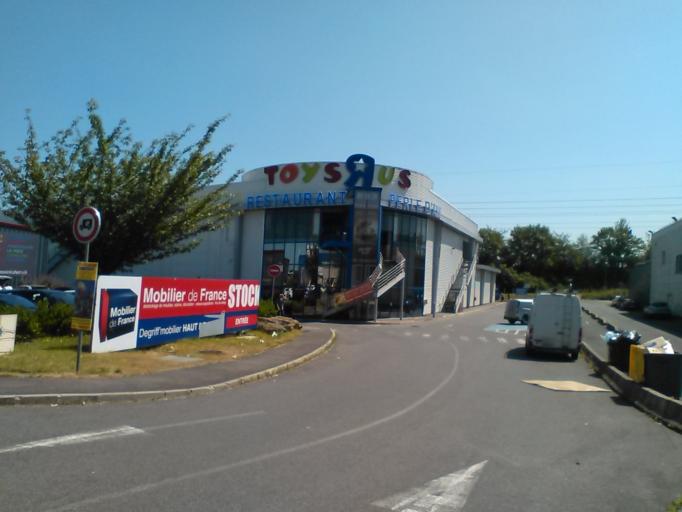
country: FR
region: Ile-de-France
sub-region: Departement de l'Essonne
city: Fleury-Merogis
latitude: 48.6243
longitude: 2.3519
